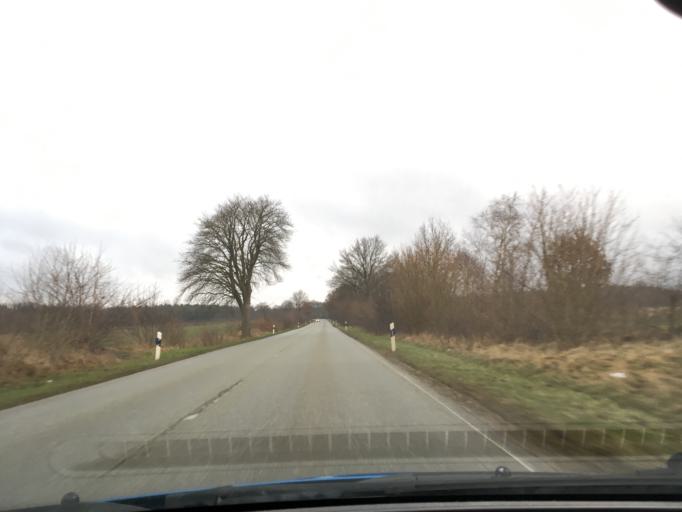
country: DE
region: Schleswig-Holstein
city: Siebeneichen
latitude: 53.5182
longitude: 10.6168
